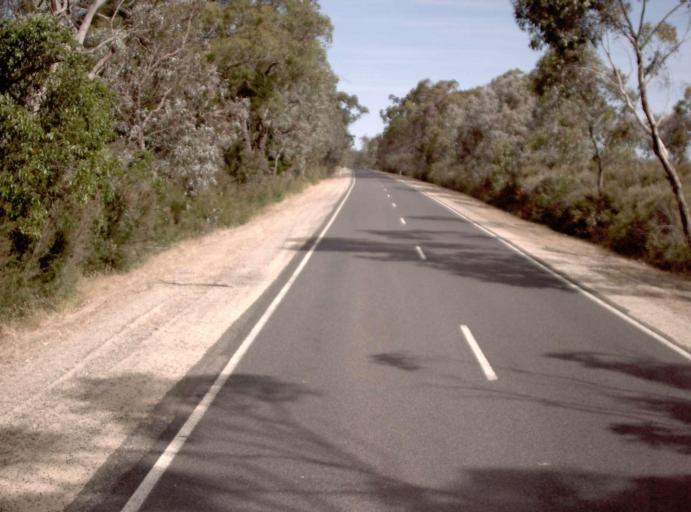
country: AU
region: Victoria
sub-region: Wellington
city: Sale
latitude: -38.2421
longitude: 147.1295
